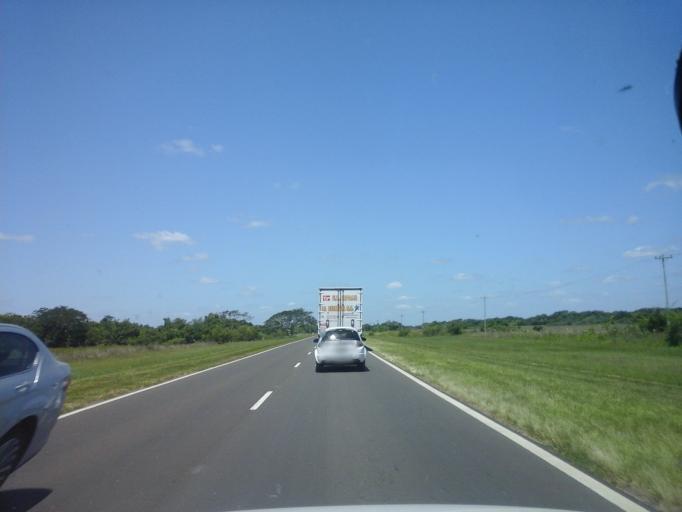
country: AR
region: Corrientes
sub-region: Departamento de Itati
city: Itati
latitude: -27.3401
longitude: -58.2127
